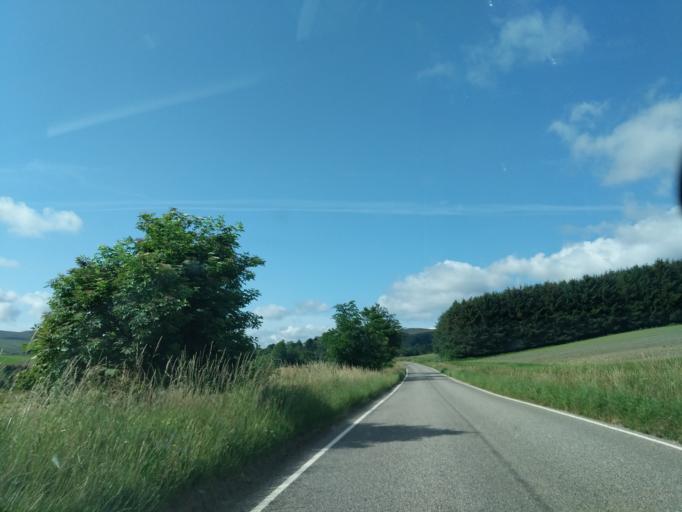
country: GB
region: Scotland
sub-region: Moray
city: Dufftown
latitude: 57.3966
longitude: -3.1996
